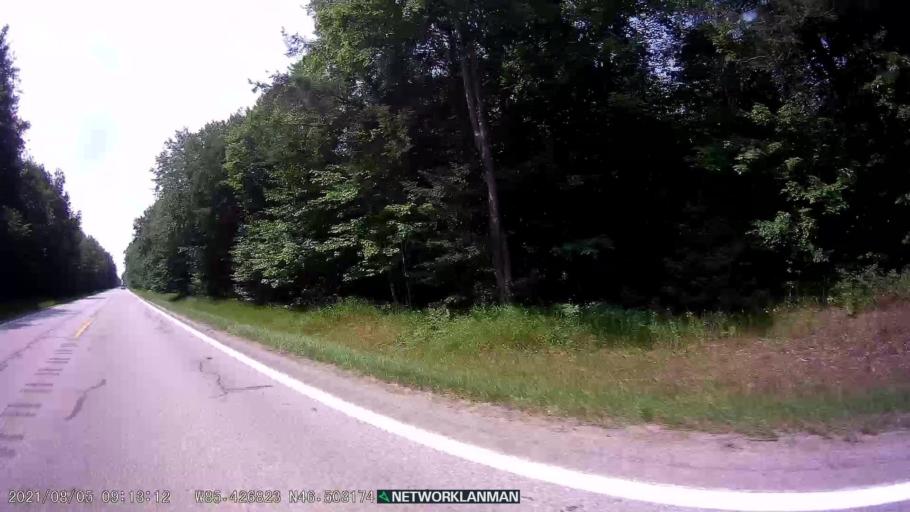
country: US
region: Michigan
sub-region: Luce County
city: Newberry
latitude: 46.5029
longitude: -85.4267
